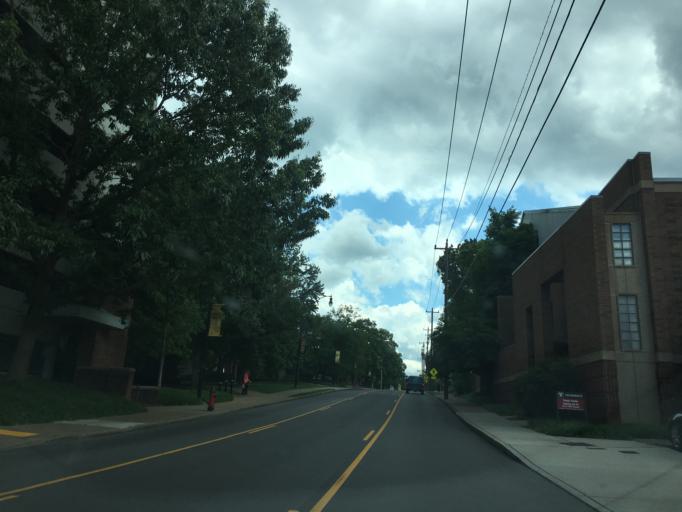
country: US
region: Tennessee
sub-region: Davidson County
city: Nashville
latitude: 36.1418
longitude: -86.8067
